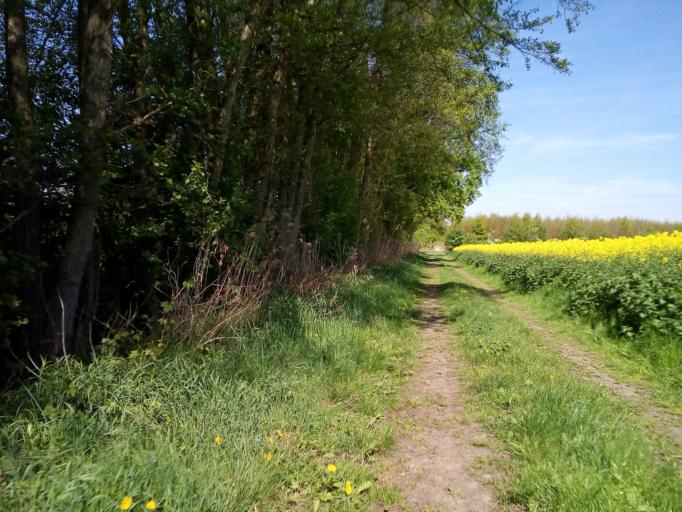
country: DE
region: Baden-Wuerttemberg
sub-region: Freiburg Region
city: Rheinau
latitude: 48.6883
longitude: 7.9720
